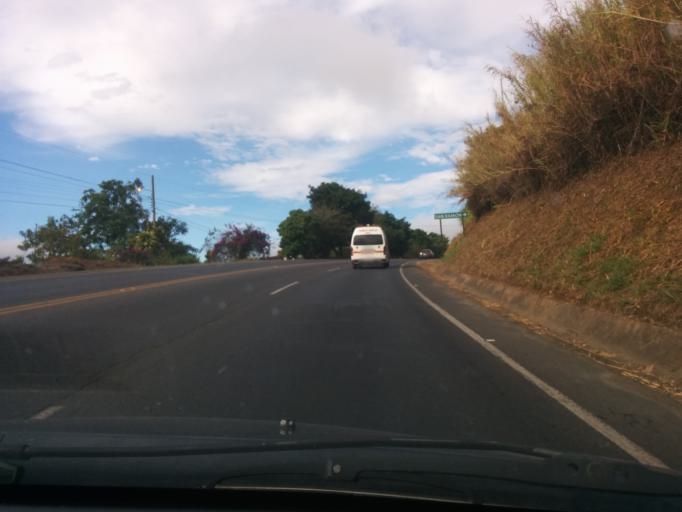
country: CR
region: Alajuela
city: San Ramon
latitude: 10.0770
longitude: -84.4671
